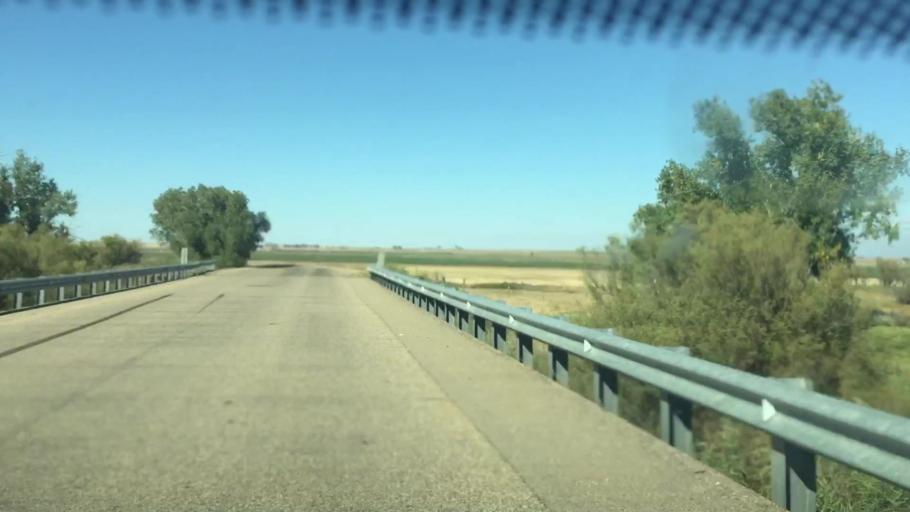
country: US
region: Colorado
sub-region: Prowers County
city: Lamar
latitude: 38.0968
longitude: -102.5195
